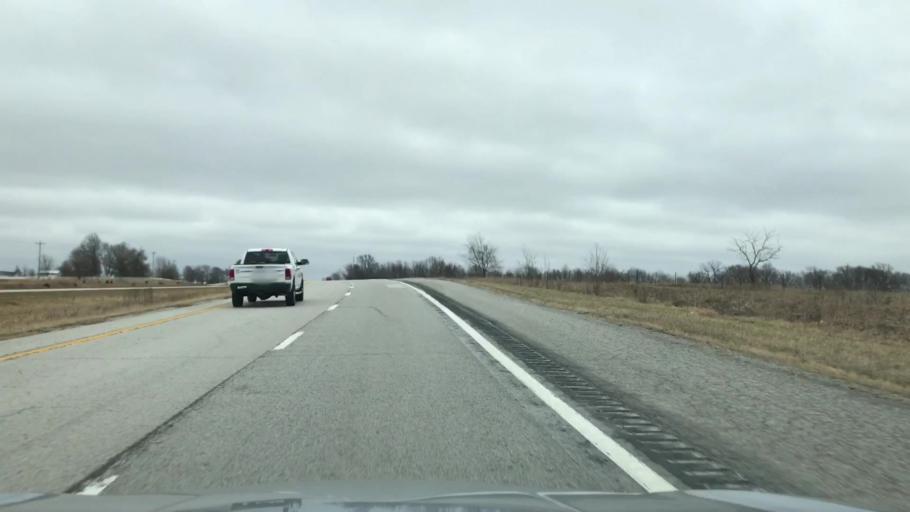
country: US
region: Missouri
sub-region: Linn County
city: Linneus
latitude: 39.7772
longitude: -93.3540
